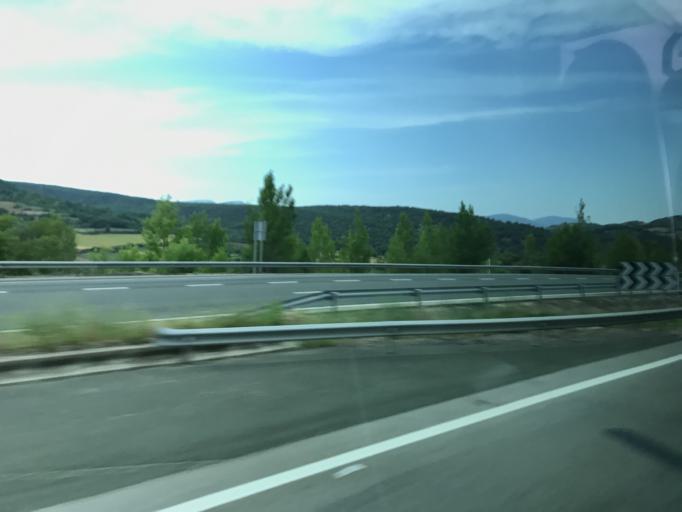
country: ES
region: Castille and Leon
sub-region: Provincia de Burgos
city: Ameyugo
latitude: 42.6475
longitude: -3.0813
